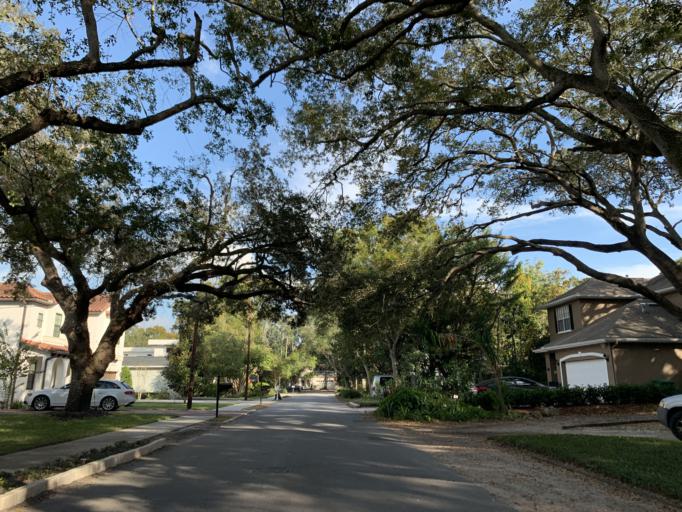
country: US
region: Florida
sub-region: Hillsborough County
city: Tampa
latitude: 27.8993
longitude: -82.4993
